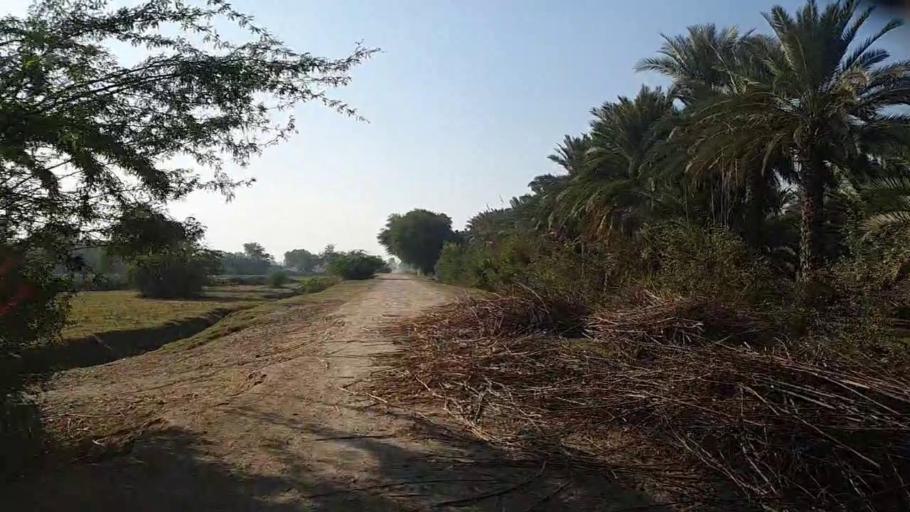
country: PK
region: Sindh
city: Ranipur
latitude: 27.2523
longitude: 68.5455
